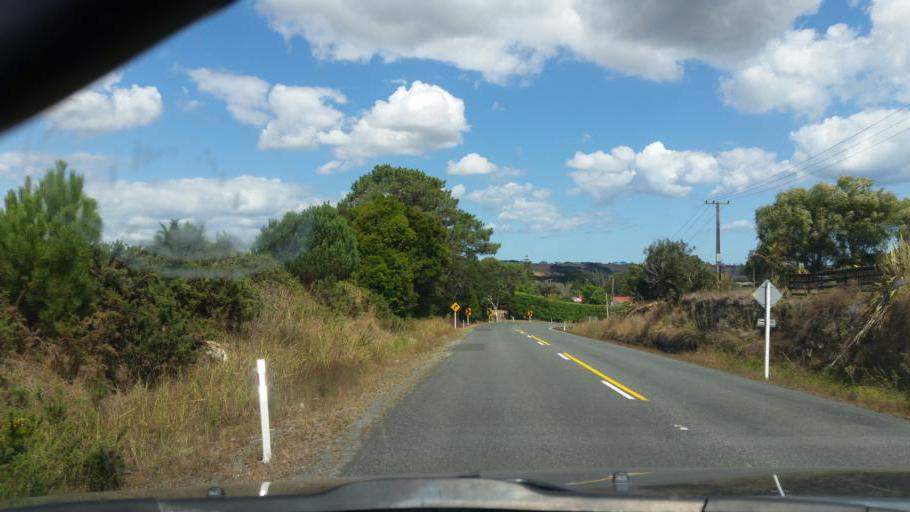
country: NZ
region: Northland
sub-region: Kaipara District
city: Dargaville
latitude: -36.0331
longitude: 173.9213
